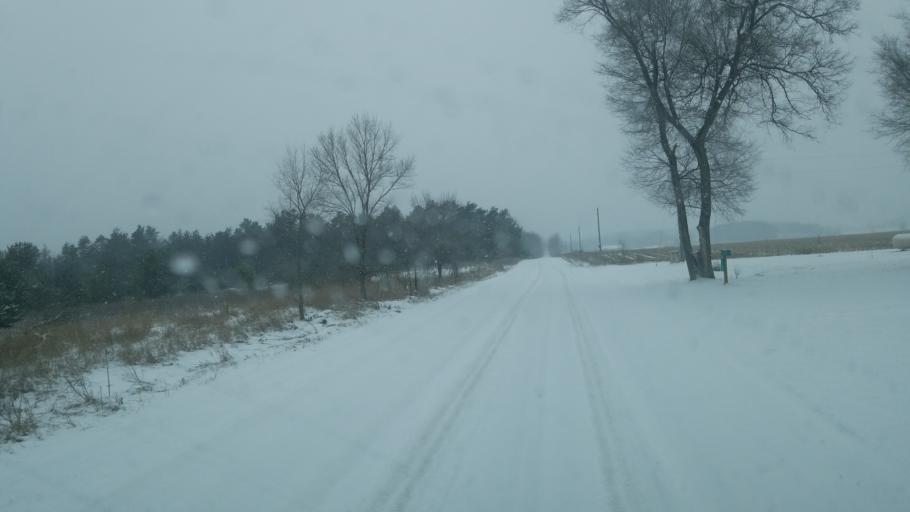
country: US
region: Michigan
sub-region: Osceola County
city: Reed City
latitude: 43.8306
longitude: -85.4140
